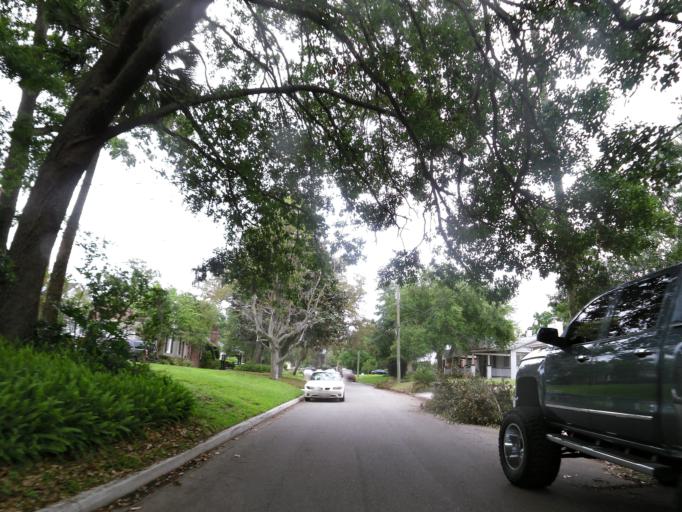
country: US
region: Florida
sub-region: Duval County
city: Jacksonville
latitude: 30.2922
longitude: -81.6463
